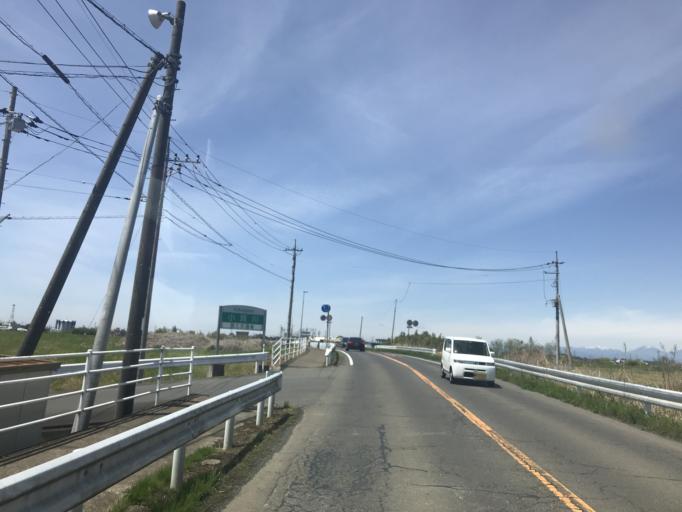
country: JP
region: Ibaraki
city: Shimodate
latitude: 36.3038
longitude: 140.0033
